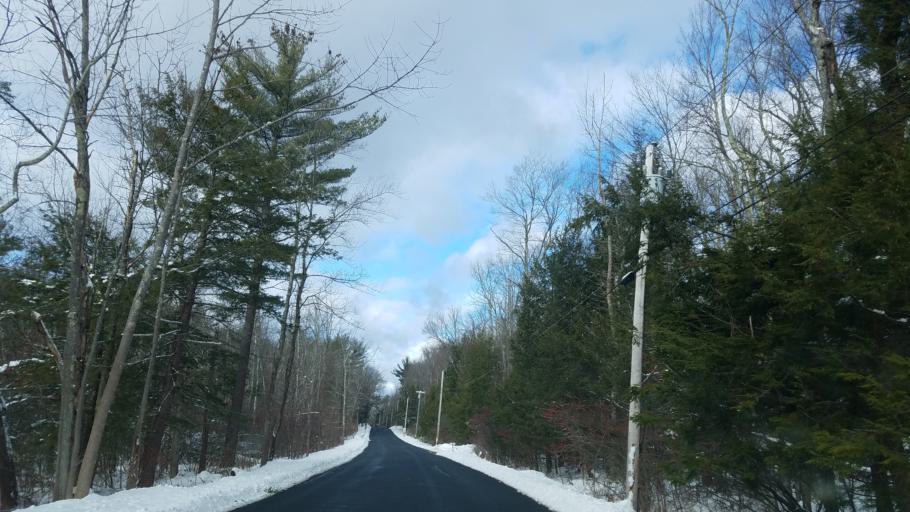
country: US
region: Connecticut
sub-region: Litchfield County
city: Winsted
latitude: 41.9831
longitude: -73.0861
